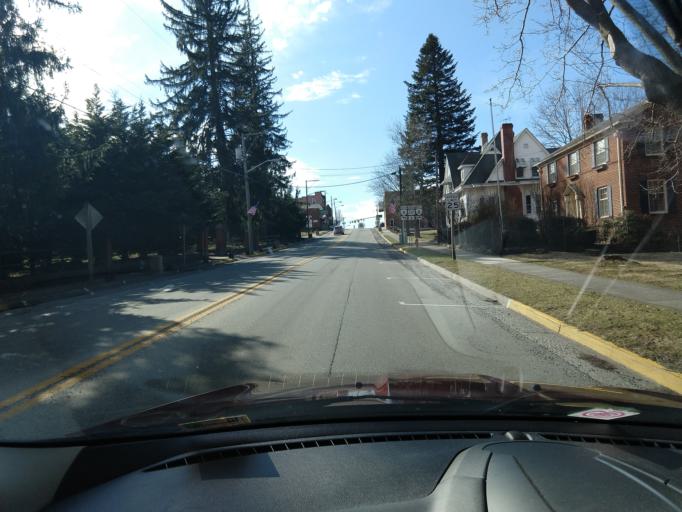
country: US
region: Virginia
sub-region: Floyd County
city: Floyd
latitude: 36.9116
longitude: -80.3180
